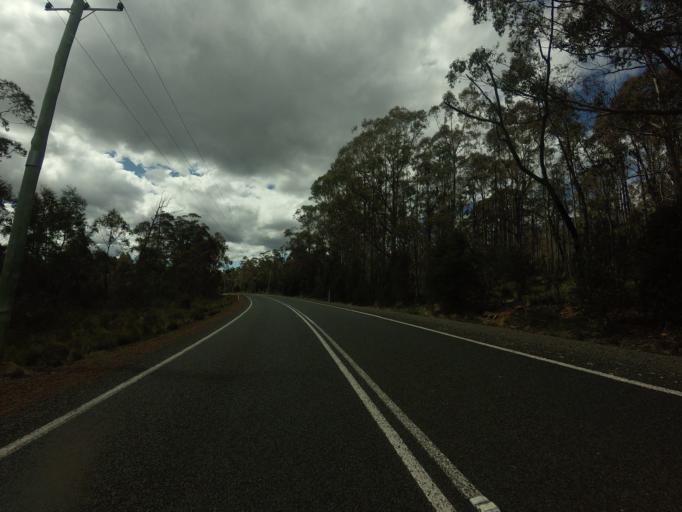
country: AU
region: Tasmania
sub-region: Northern Midlands
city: Evandale
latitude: -42.0077
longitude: 147.7238
